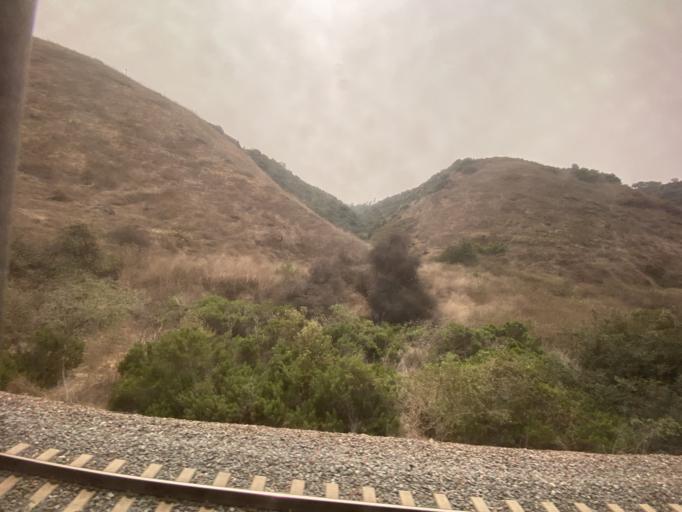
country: US
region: California
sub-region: San Diego County
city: La Jolla
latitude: 32.8870
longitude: -117.2060
